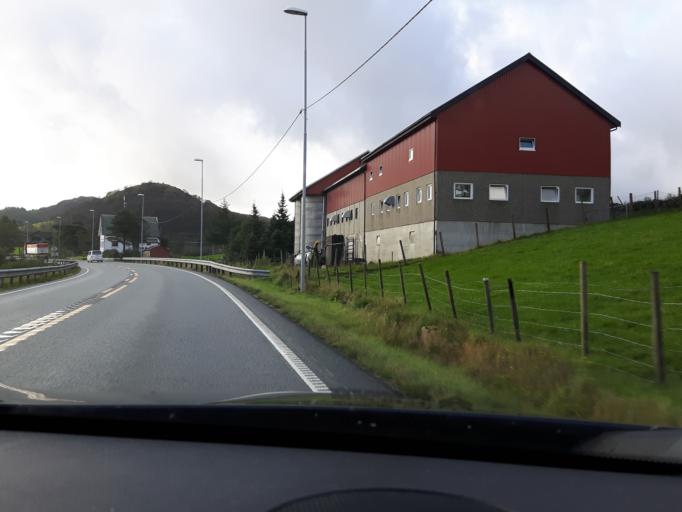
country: NO
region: Rogaland
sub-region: Bjerkreim
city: Vikesa
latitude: 58.6684
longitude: 5.9849
